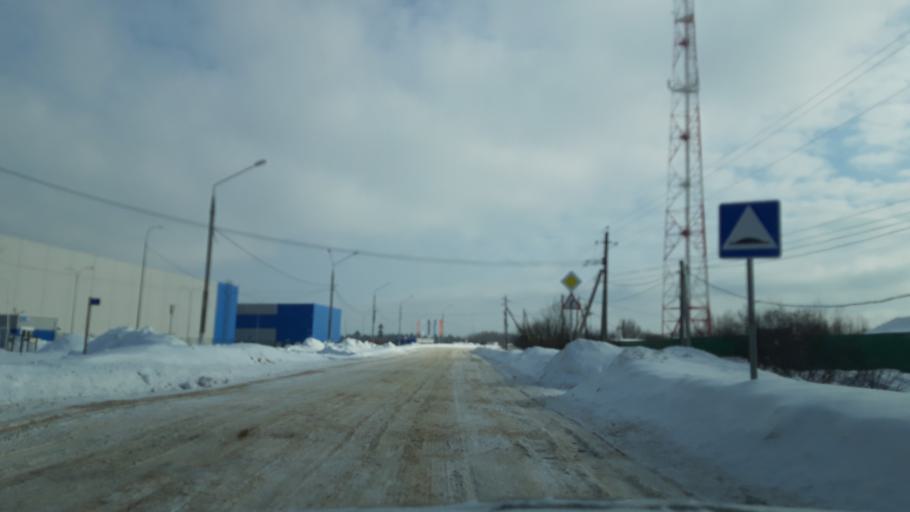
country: RU
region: Moskovskaya
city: Yermolino
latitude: 56.1432
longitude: 37.3774
